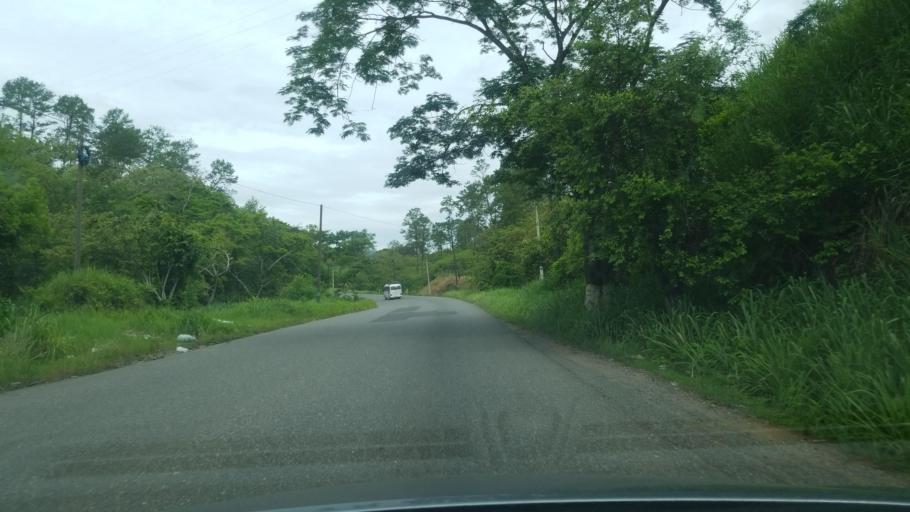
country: HN
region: Santa Barbara
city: San Marcos
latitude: 15.3044
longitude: -88.4497
